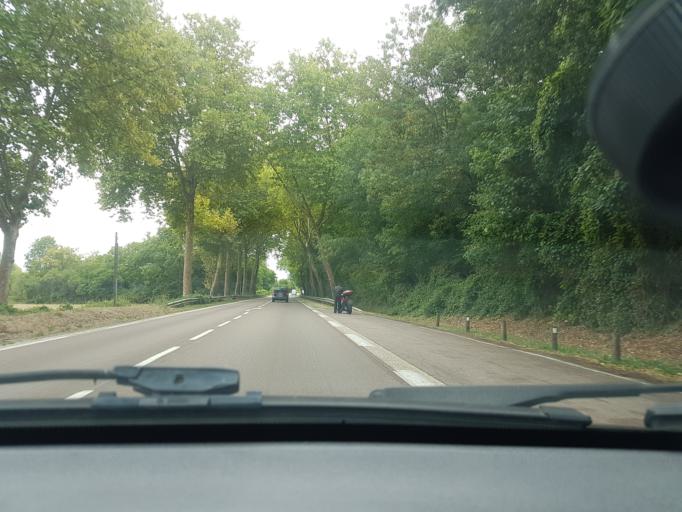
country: FR
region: Bourgogne
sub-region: Departement de l'Yonne
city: Champs-sur-Yonne
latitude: 47.7125
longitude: 3.6216
